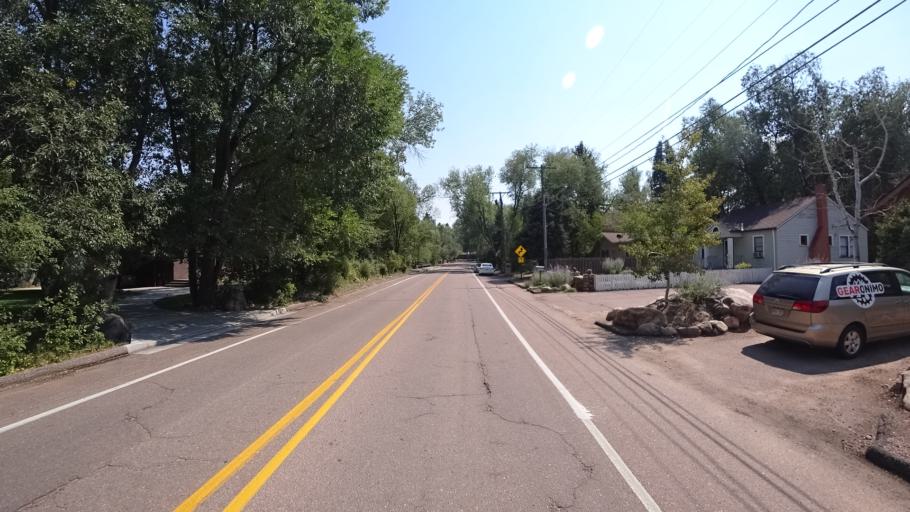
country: US
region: Colorado
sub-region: El Paso County
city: Colorado Springs
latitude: 38.8035
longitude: -104.8349
